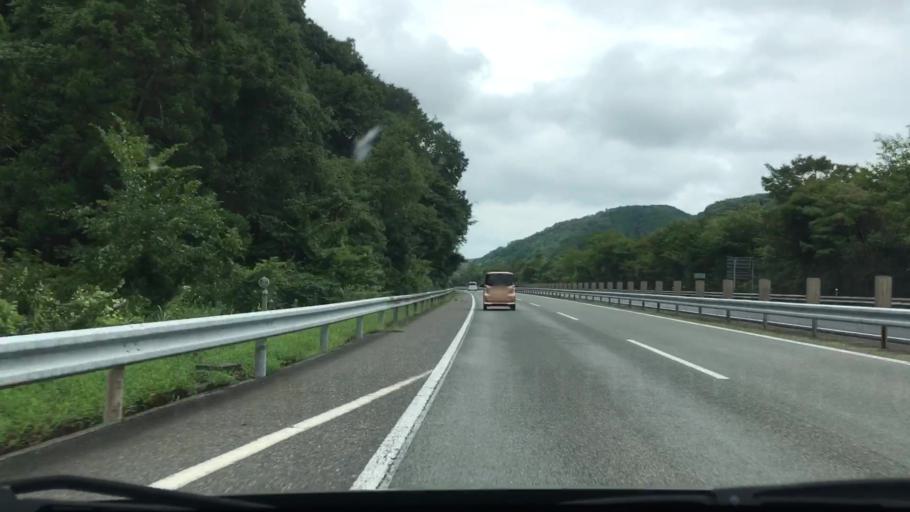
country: JP
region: Hiroshima
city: Miyoshi
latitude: 34.7682
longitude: 132.7999
